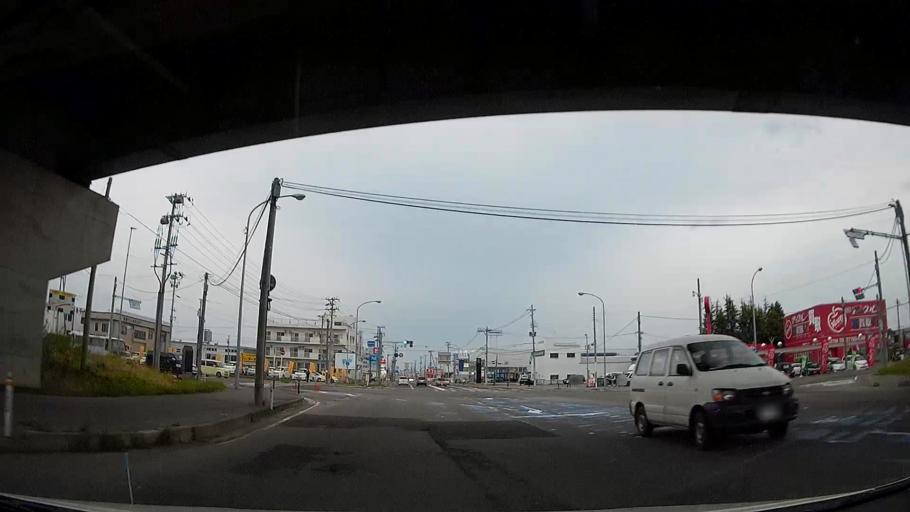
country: JP
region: Aomori
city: Aomori Shi
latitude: 40.7949
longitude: 140.7591
